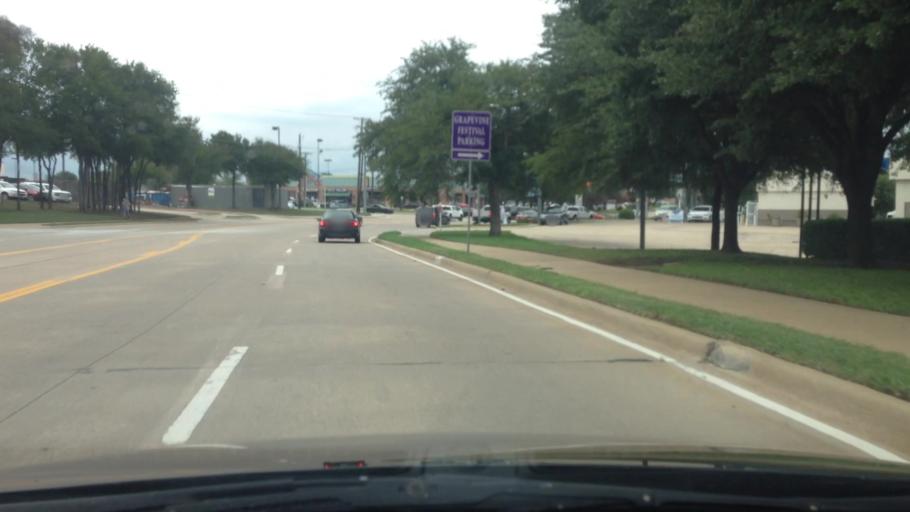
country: US
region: Texas
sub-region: Tarrant County
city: Grapevine
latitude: 32.9399
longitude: -97.0989
